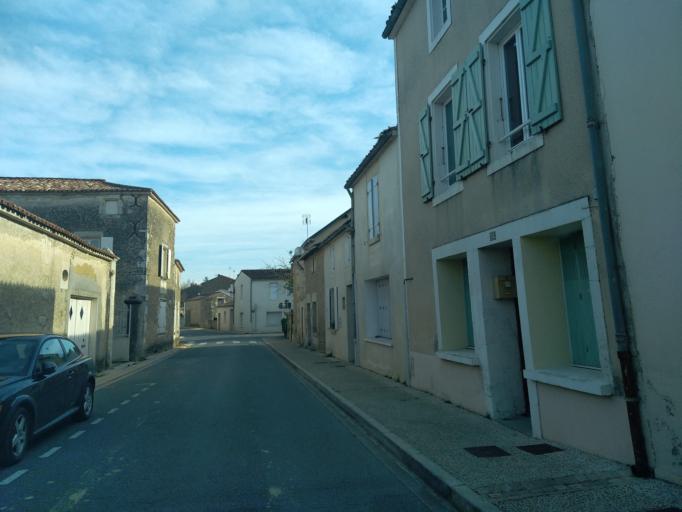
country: FR
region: Pays de la Loire
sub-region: Departement de la Vendee
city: Maillezais
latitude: 46.3723
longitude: -0.7424
